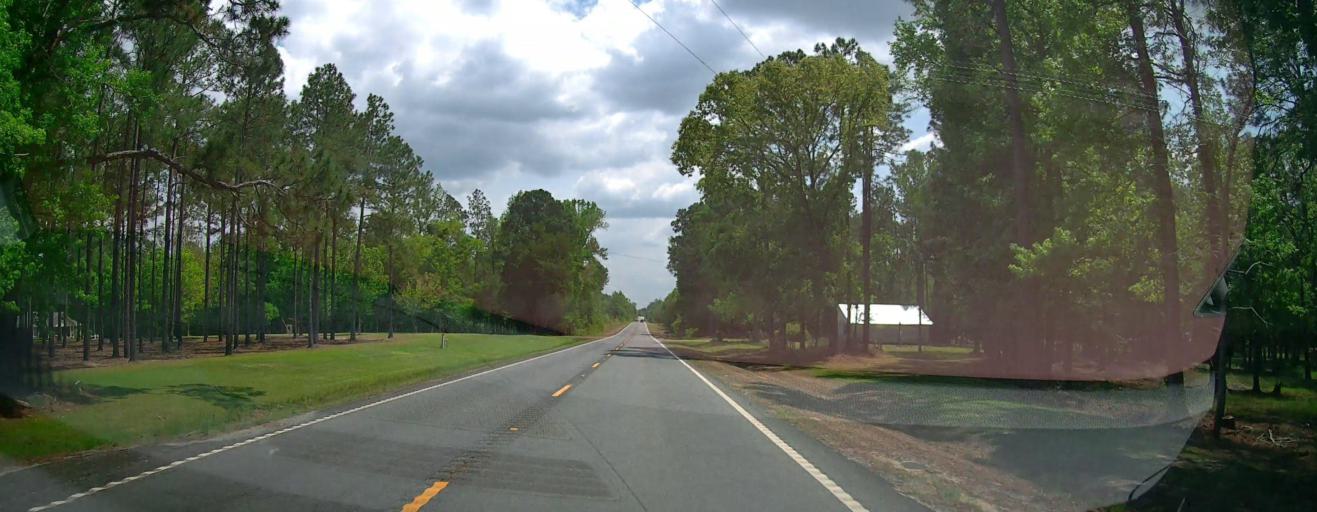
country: US
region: Georgia
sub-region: Treutlen County
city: Soperton
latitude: 32.3975
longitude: -82.6029
